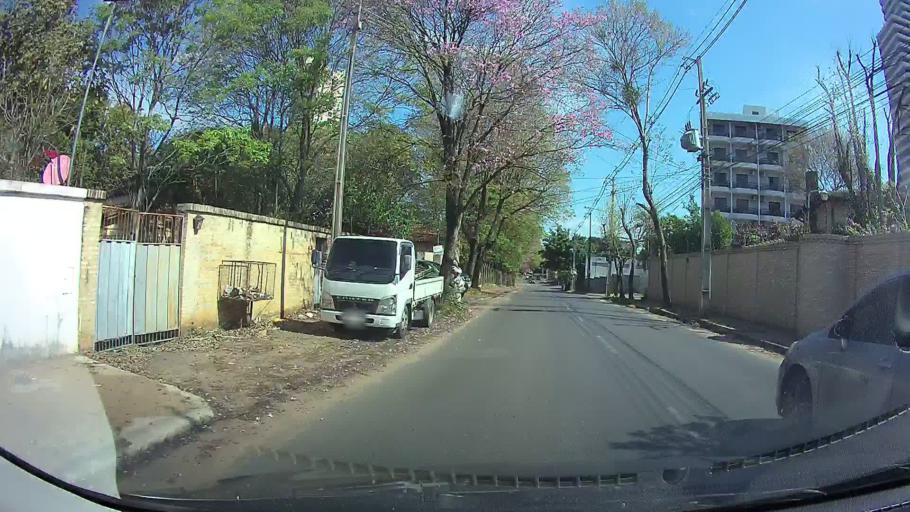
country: PY
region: Central
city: Fernando de la Mora
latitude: -25.2867
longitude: -57.5549
